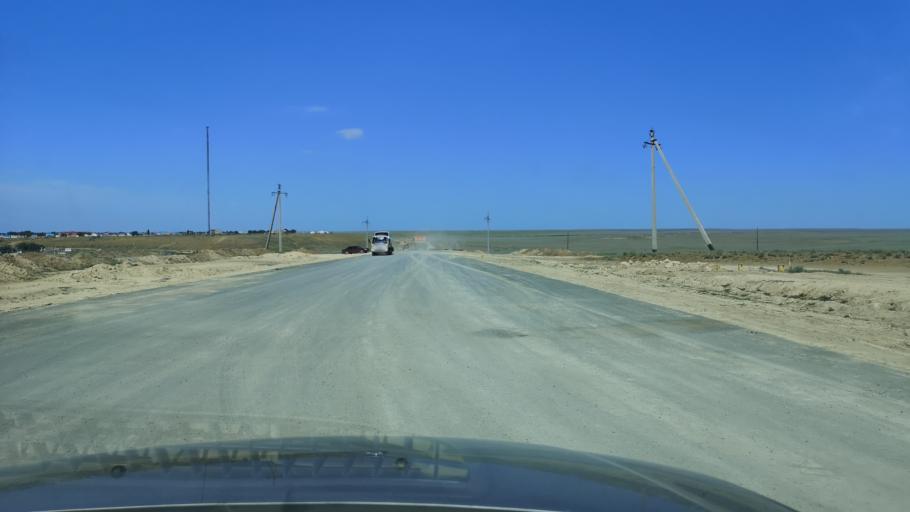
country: KZ
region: Aqtoebe
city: Bayganin
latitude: 48.6707
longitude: 55.8689
